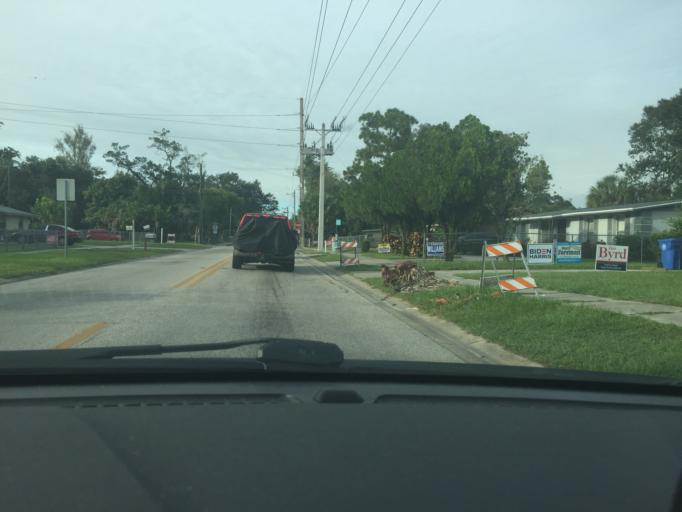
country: US
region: Florida
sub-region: Manatee County
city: Samoset
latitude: 27.4908
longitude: -82.5303
